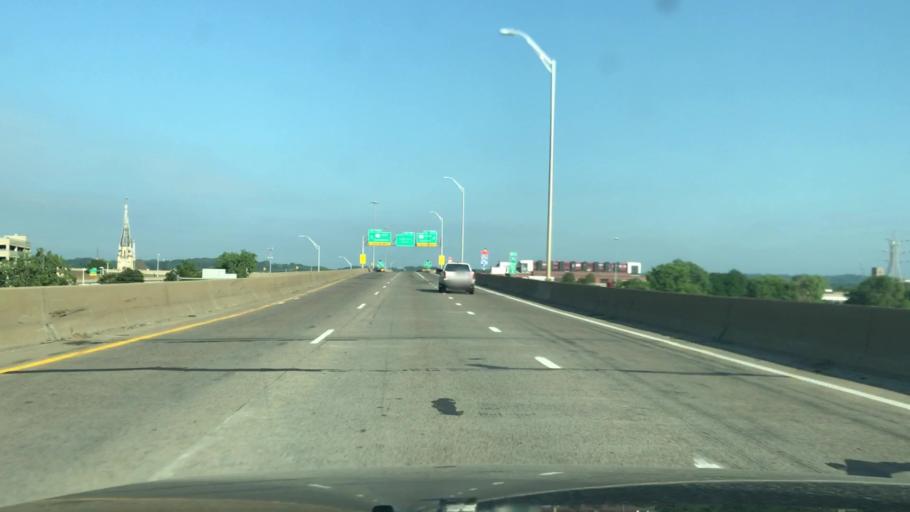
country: US
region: Michigan
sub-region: Kent County
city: Grand Rapids
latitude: 42.9723
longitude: -85.6729
